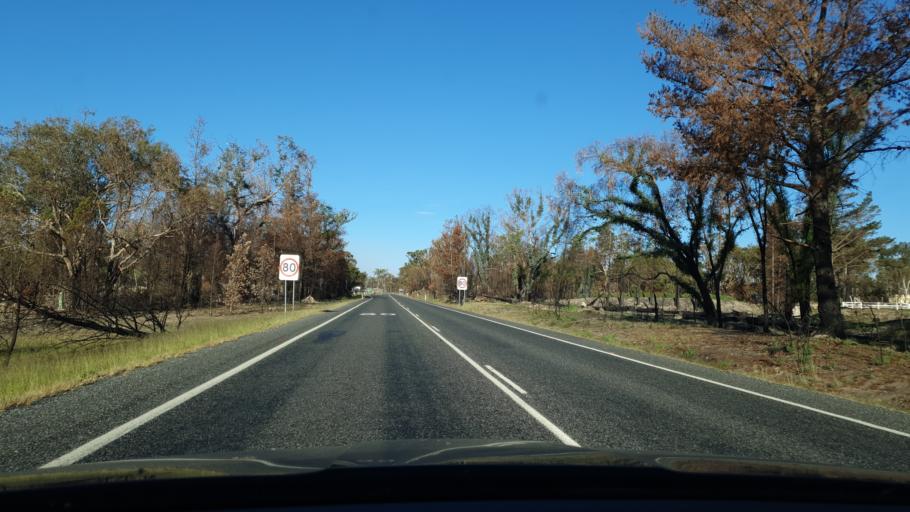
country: AU
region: Queensland
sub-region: Southern Downs
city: Stanthorpe
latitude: -28.6389
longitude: 151.9443
